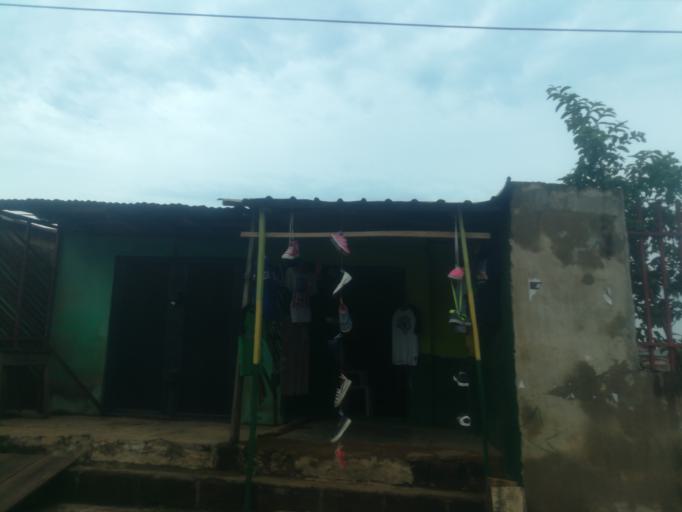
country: NG
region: Oyo
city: Ibadan
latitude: 7.3939
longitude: 3.9482
